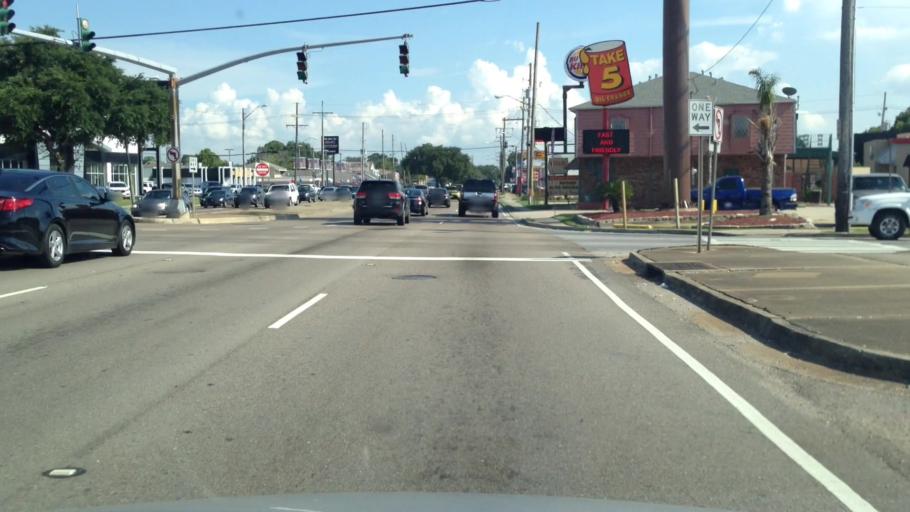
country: US
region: Louisiana
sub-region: Jefferson Parish
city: Metairie Terrace
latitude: 29.9940
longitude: -90.1818
